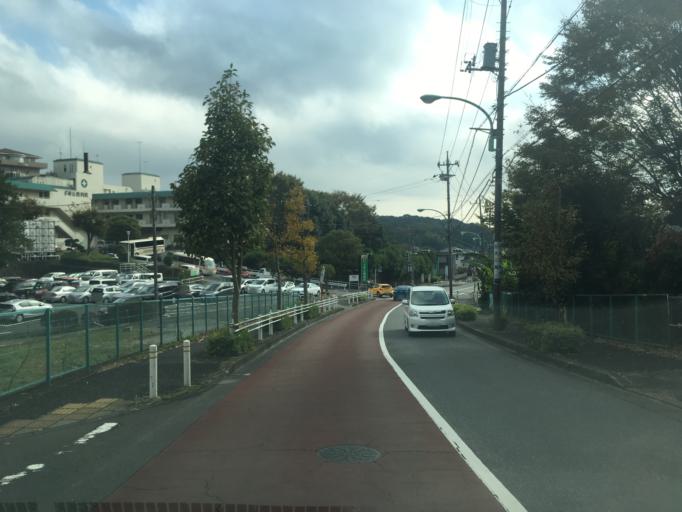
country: JP
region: Tokyo
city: Hino
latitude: 35.6055
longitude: 139.4206
